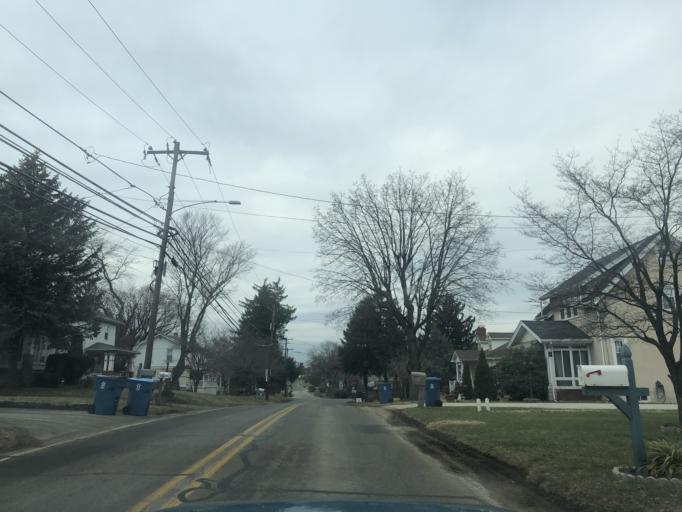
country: US
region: Pennsylvania
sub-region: Montgomery County
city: Bridgeport
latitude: 40.0935
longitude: -75.3494
